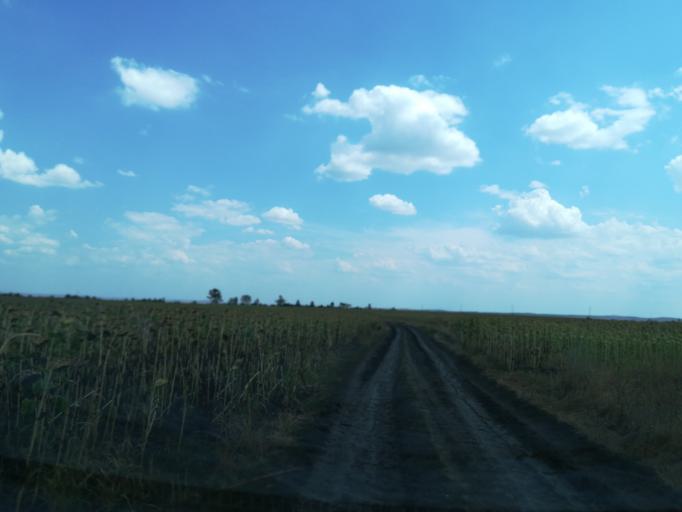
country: BG
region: Khaskovo
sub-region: Obshtina Mineralni Bani
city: Mineralni Bani
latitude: 42.0045
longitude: 25.2060
